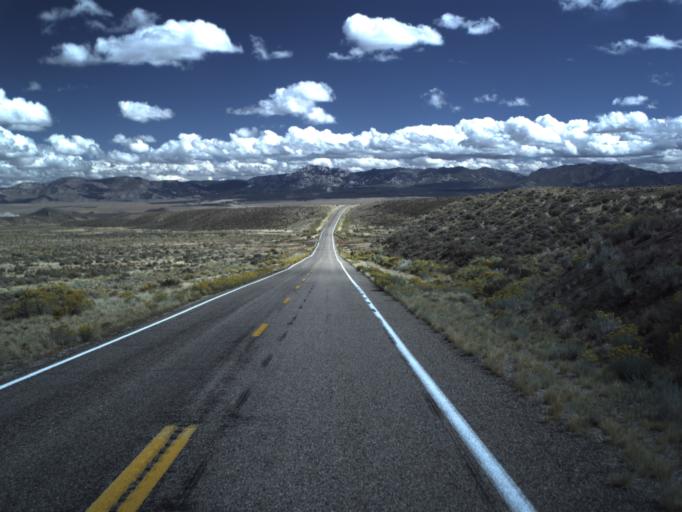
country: US
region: Utah
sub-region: Beaver County
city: Milford
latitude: 38.4399
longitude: -113.1580
